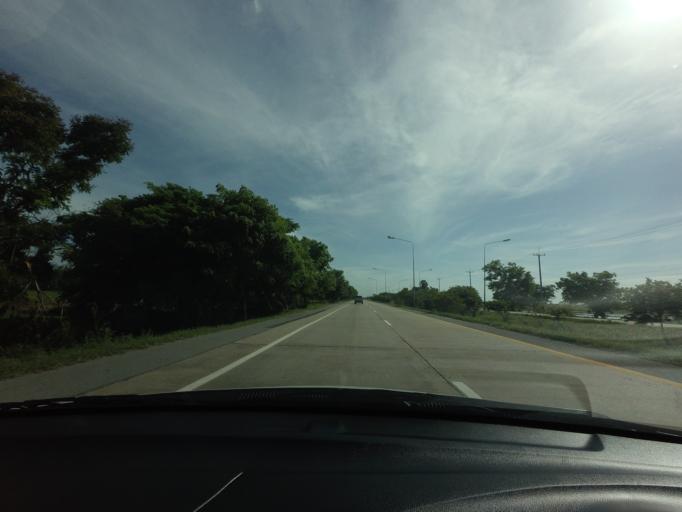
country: TH
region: Suphan Buri
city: Suphan Buri
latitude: 14.4849
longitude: 100.0429
